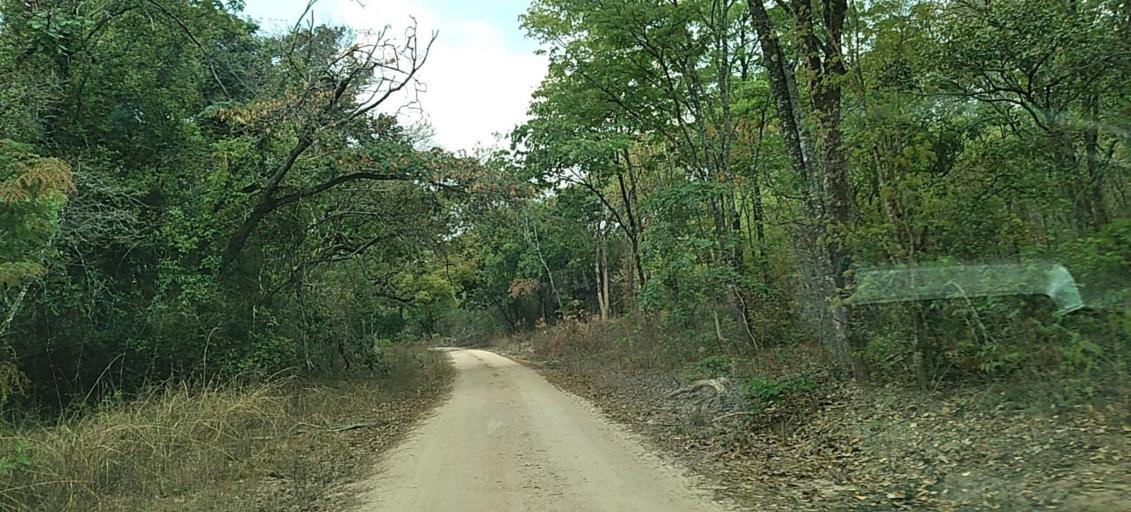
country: ZM
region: Copperbelt
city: Chingola
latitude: -12.7546
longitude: 27.7130
